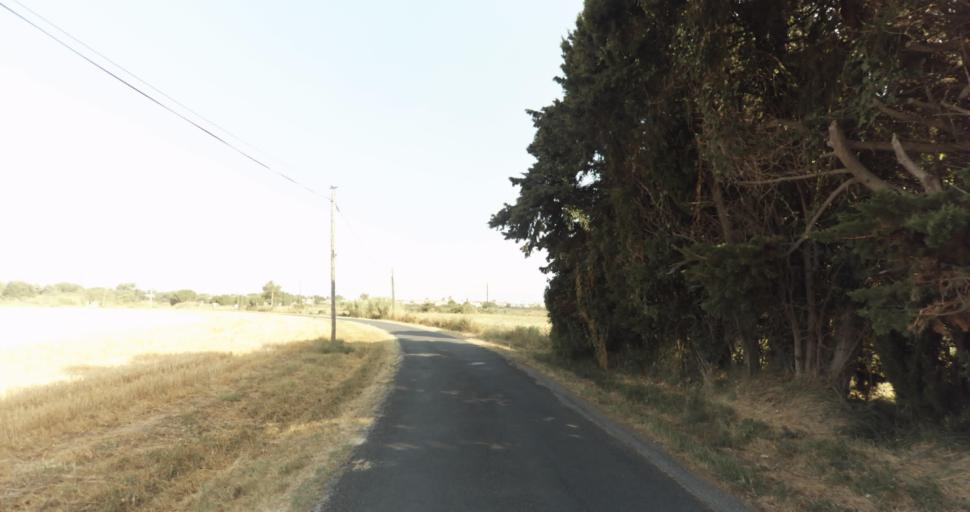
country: FR
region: Languedoc-Roussillon
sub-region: Departement des Pyrenees-Orientales
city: Latour-Bas-Elne
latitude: 42.6108
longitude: 3.0186
